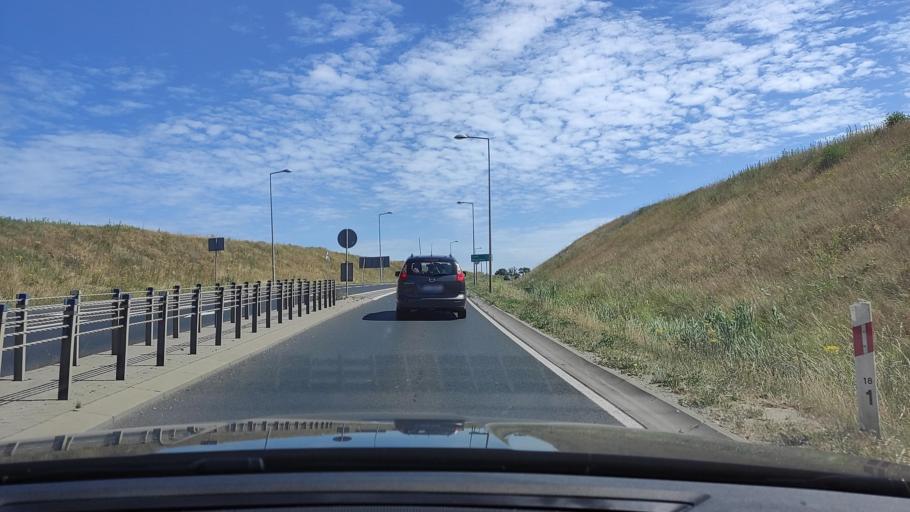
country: PL
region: Greater Poland Voivodeship
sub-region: Powiat poznanski
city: Murowana Goslina
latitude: 52.5834
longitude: 16.9848
